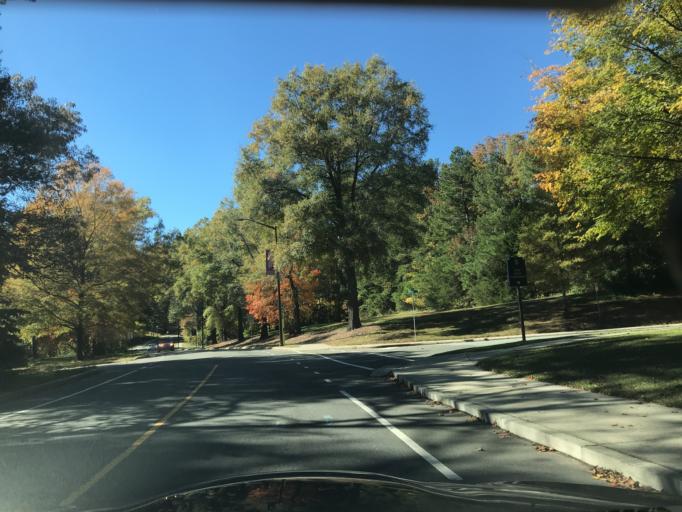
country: US
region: North Carolina
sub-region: Durham County
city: Durham
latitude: 36.0004
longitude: -78.9257
